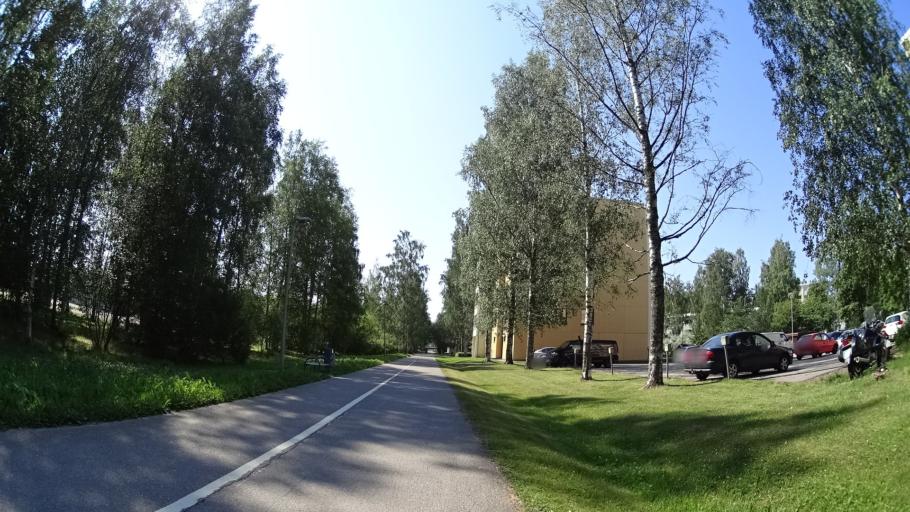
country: FI
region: Uusimaa
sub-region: Helsinki
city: Kerava
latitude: 60.3925
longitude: 25.0944
